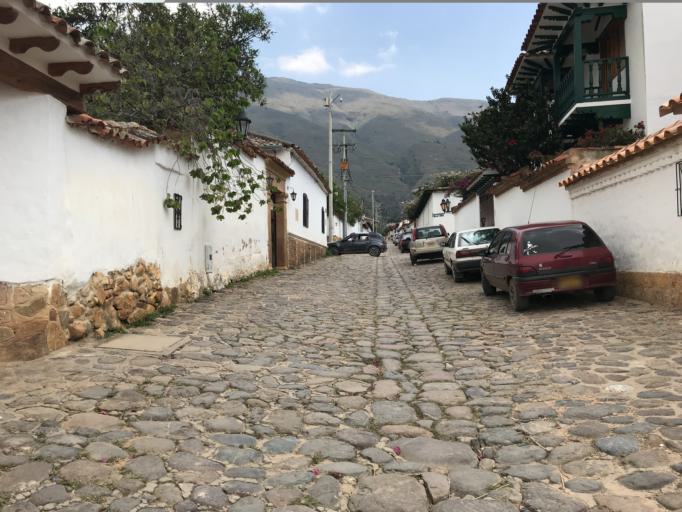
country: CO
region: Boyaca
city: Villa de Leiva
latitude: 5.6339
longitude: -73.5216
